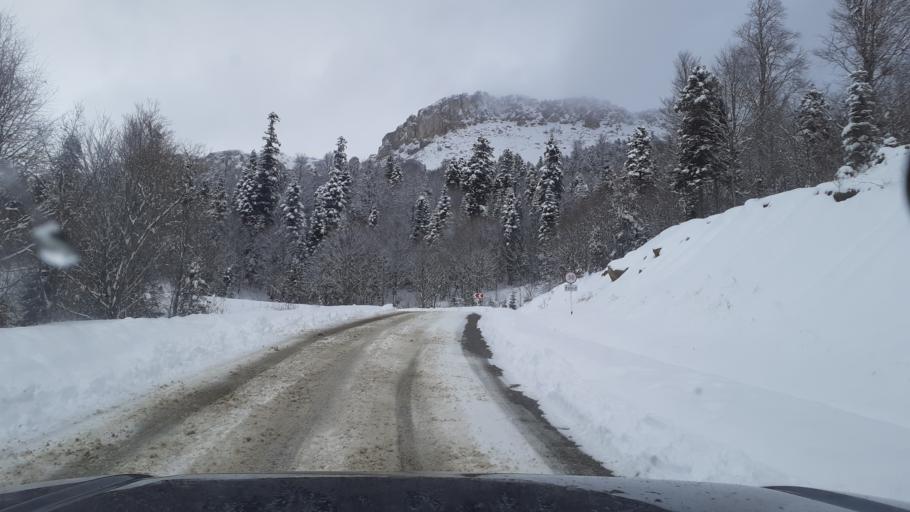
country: RU
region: Adygeya
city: Kamennomostskiy
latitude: 44.0088
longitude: 40.0104
